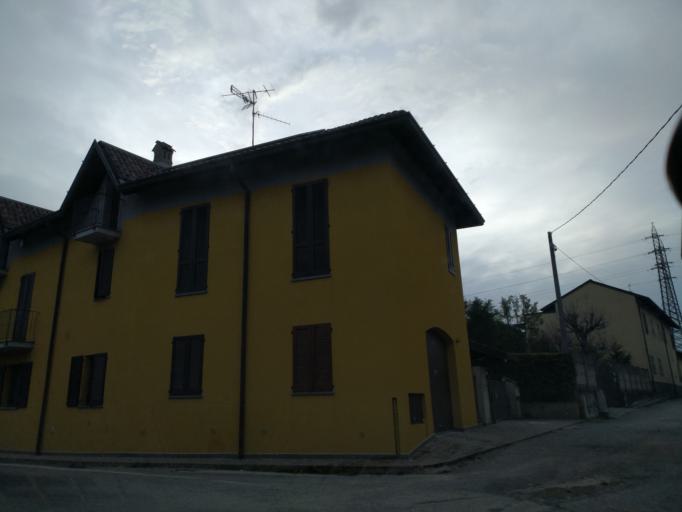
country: IT
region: Lombardy
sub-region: Provincia di Monza e Brianza
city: Verano Brianza
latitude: 45.7032
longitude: 9.2204
